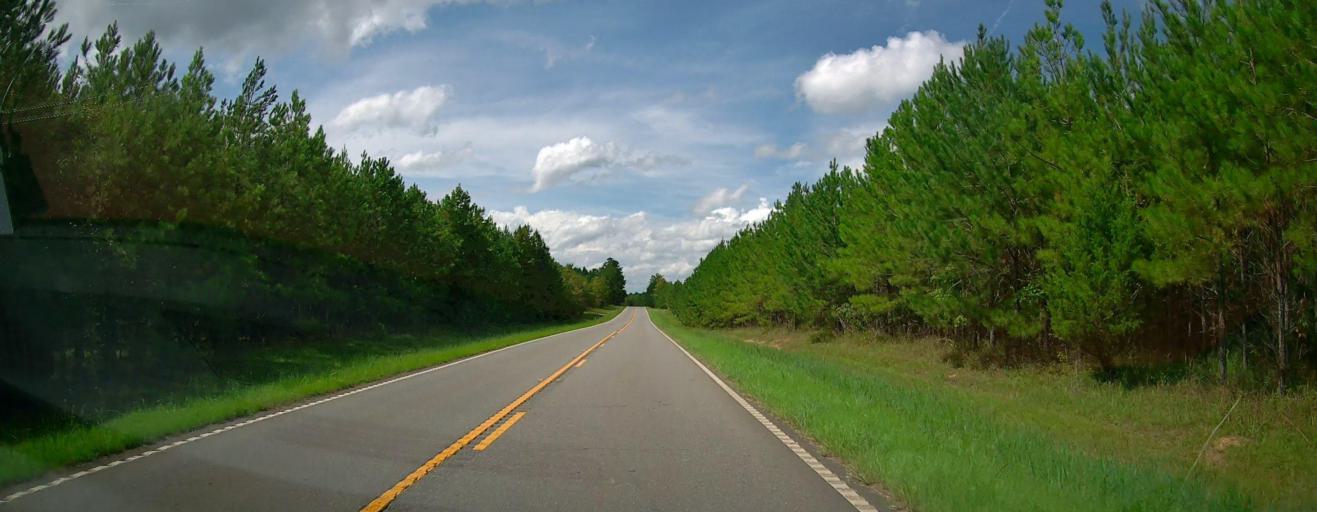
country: US
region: Georgia
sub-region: Talbot County
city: Talbotton
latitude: 32.6600
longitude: -84.5116
